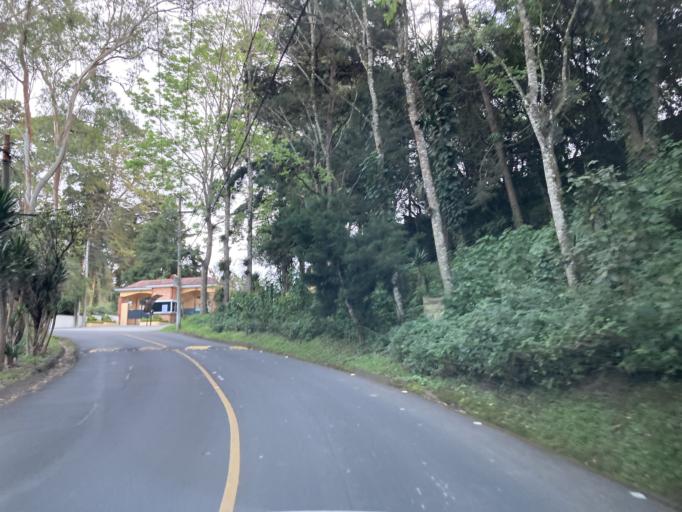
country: GT
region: Guatemala
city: Santa Catarina Pinula
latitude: 14.5562
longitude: -90.4617
